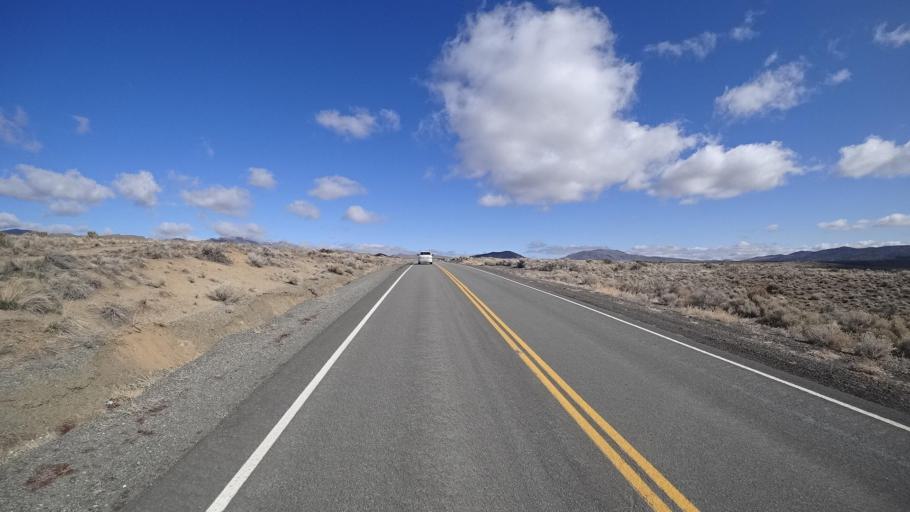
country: US
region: Nevada
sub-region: Washoe County
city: Cold Springs
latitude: 39.6776
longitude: -119.9224
